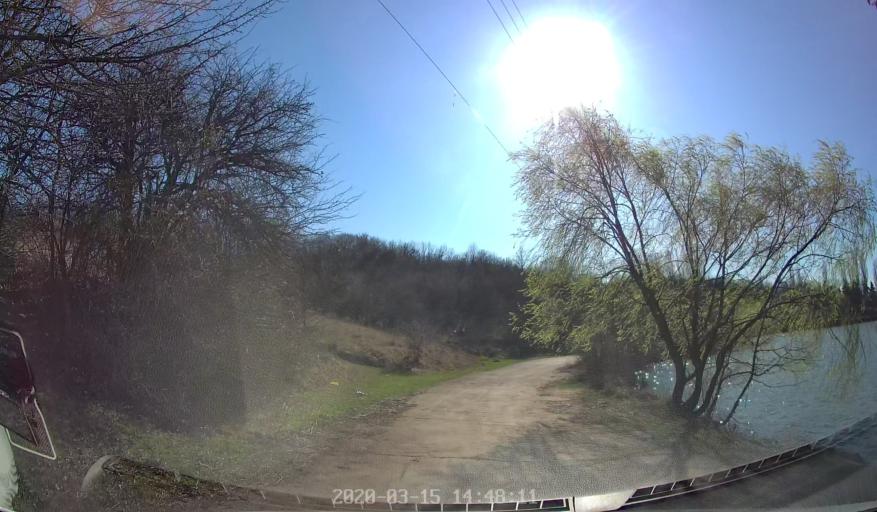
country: MD
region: Orhei
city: Orhei
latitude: 47.2806
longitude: 28.8316
